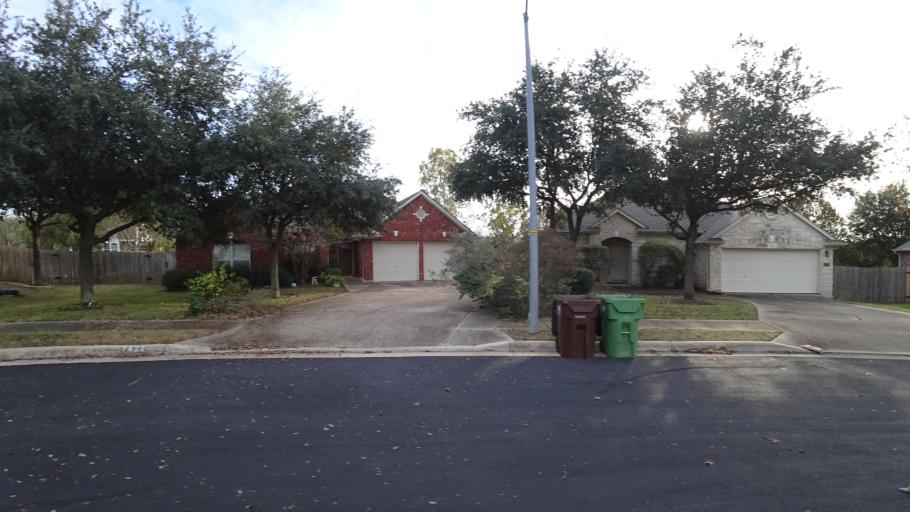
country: US
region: Texas
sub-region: Williamson County
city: Brushy Creek
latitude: 30.5161
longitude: -97.7324
